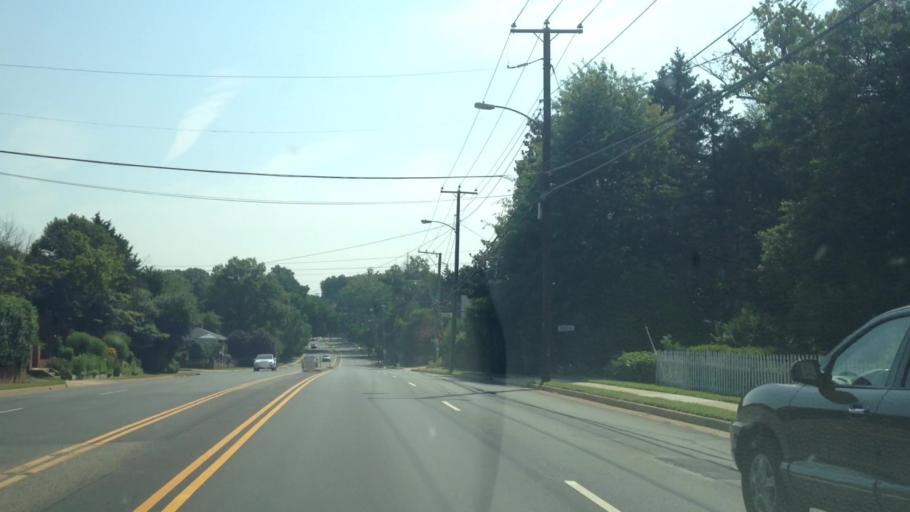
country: US
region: Virginia
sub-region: Fairfax County
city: Seven Corners
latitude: 38.8926
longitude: -77.1514
